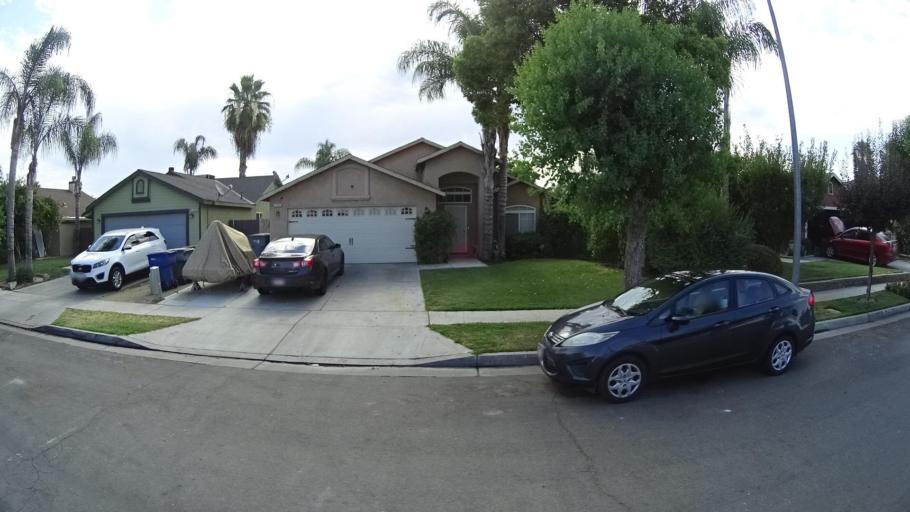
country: US
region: California
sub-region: Fresno County
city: Sunnyside
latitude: 36.7599
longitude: -119.7169
